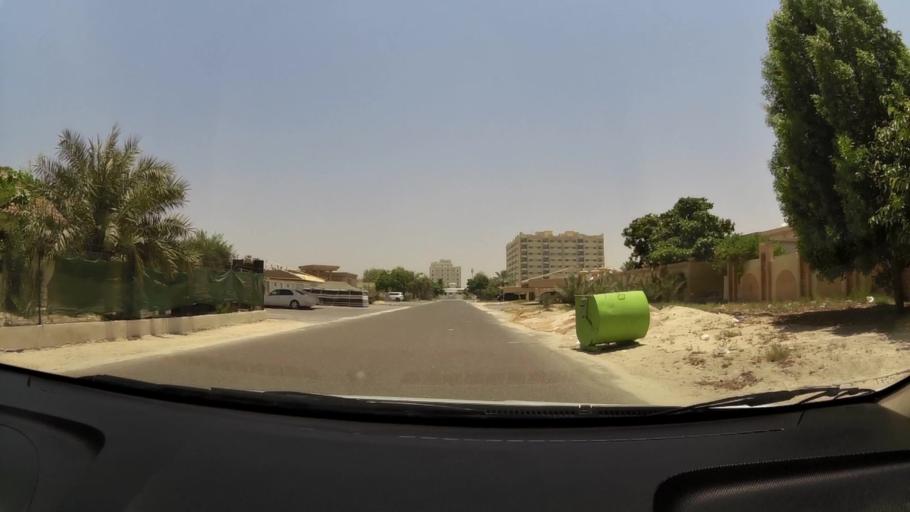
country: AE
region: Umm al Qaywayn
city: Umm al Qaywayn
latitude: 25.5425
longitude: 55.5378
